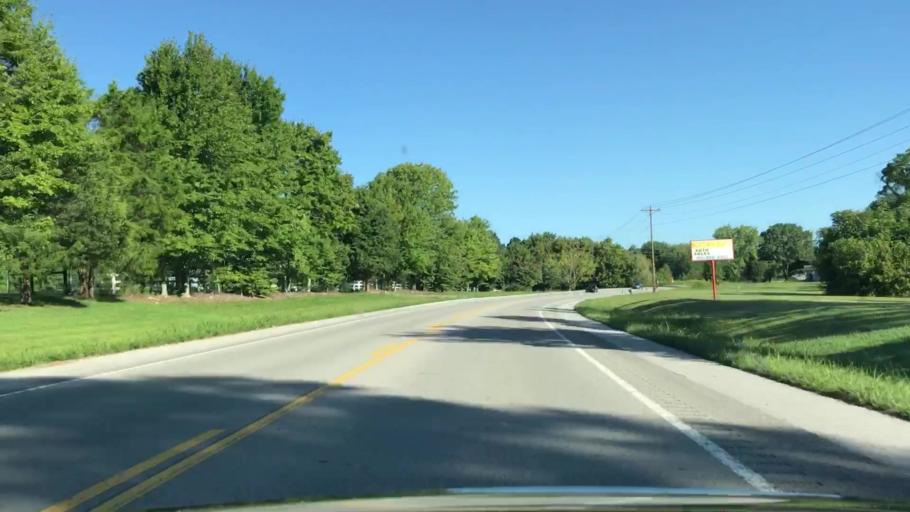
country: US
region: Tennessee
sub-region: Jackson County
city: Dodson Branch
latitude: 36.2690
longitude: -85.6168
